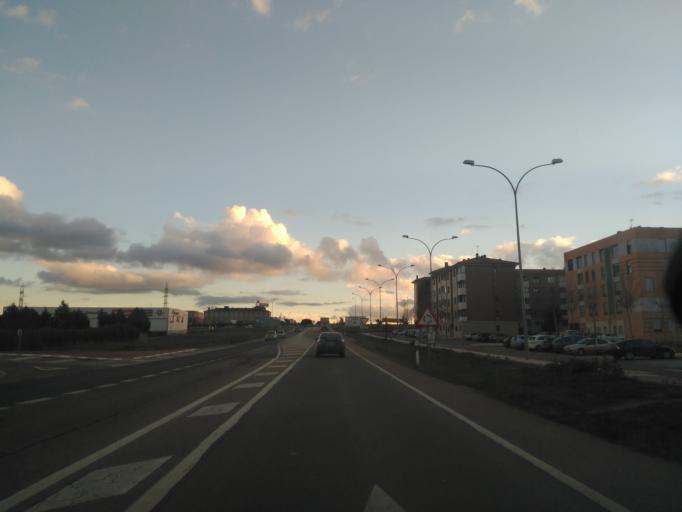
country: ES
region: Castille and Leon
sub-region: Provincia de Salamanca
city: Carbajosa de la Sagrada
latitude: 40.9438
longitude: -5.6694
